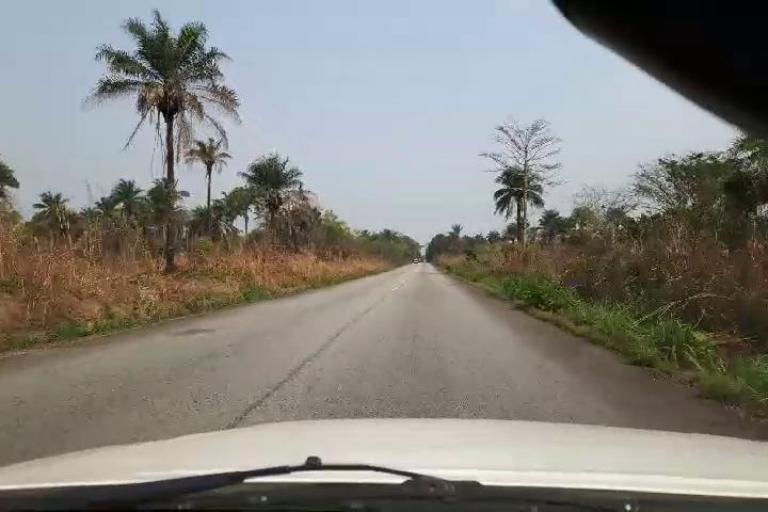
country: SL
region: Southern Province
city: Baiima
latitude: 8.1369
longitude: -11.8952
